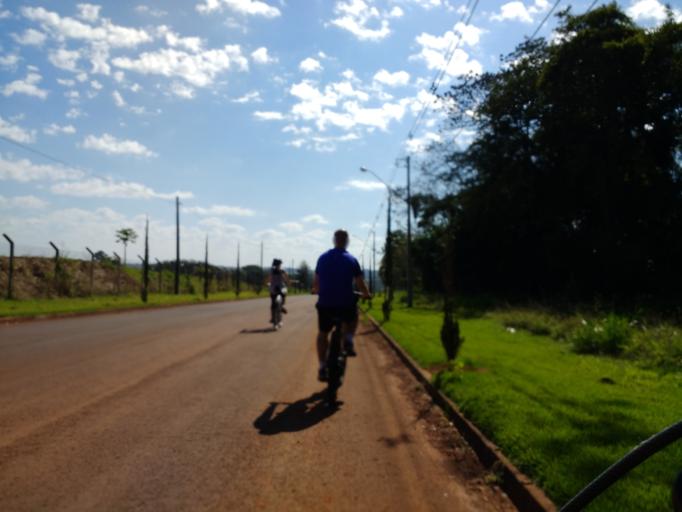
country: BR
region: Parana
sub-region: Londrina
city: Londrina
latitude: -23.3653
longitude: -51.1955
